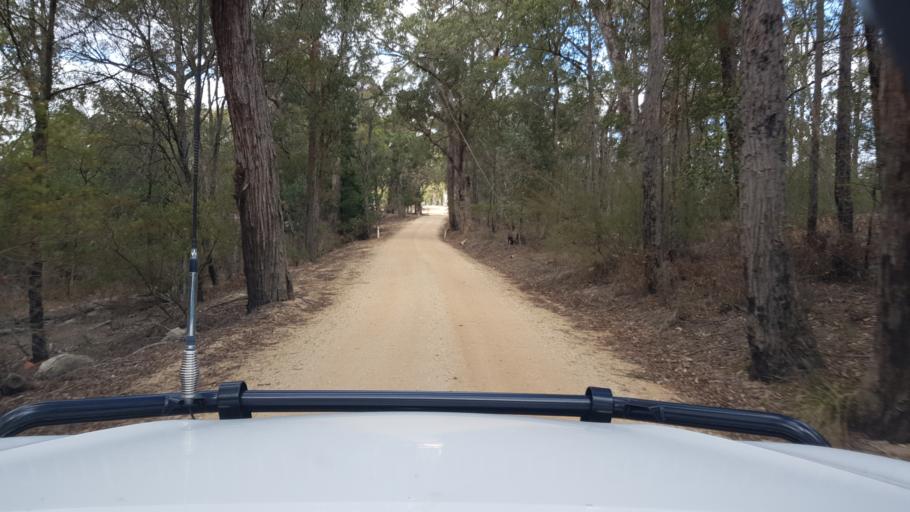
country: AU
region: Victoria
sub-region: East Gippsland
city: Bairnsdale
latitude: -37.7495
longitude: 147.6063
